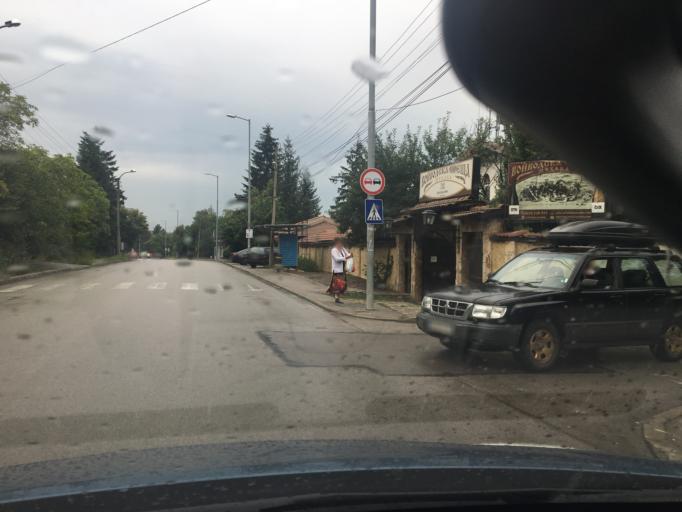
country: BG
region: Sofia-Capital
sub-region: Stolichna Obshtina
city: Sofia
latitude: 42.6343
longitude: 23.3042
